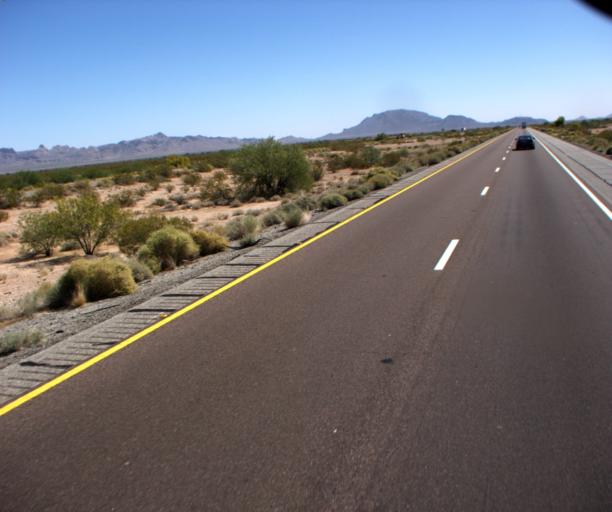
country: US
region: Arizona
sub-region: La Paz County
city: Salome
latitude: 33.5478
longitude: -113.2156
